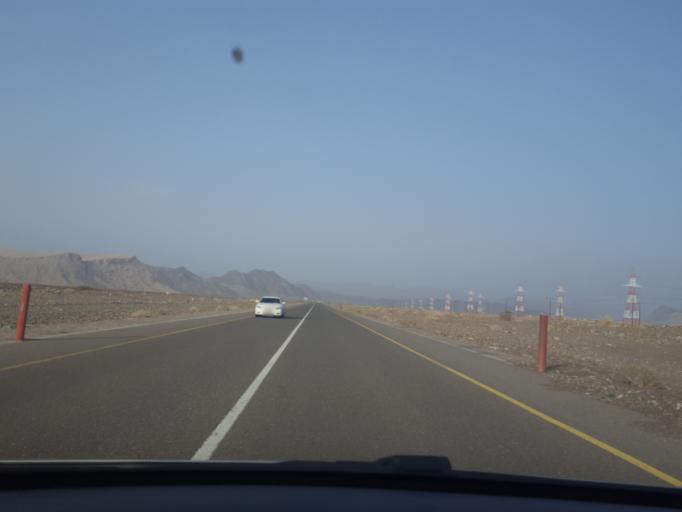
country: AE
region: Abu Dhabi
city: Al Ain
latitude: 24.0409
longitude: 56.0249
